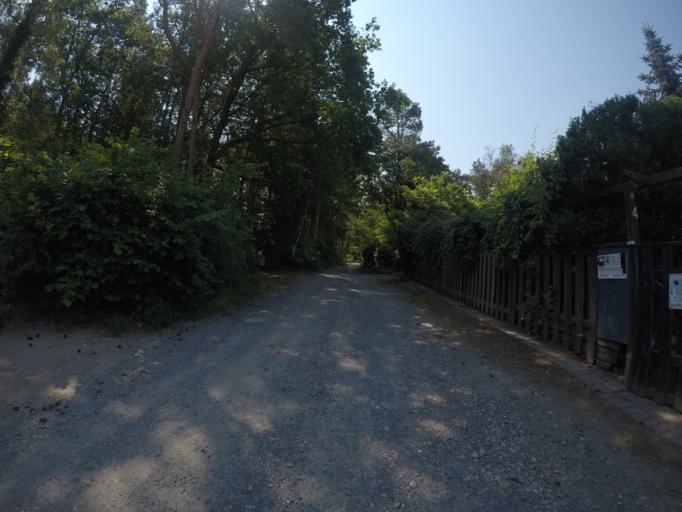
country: DE
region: Lower Saxony
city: Buchholz in der Nordheide
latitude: 53.3089
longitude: 9.8190
